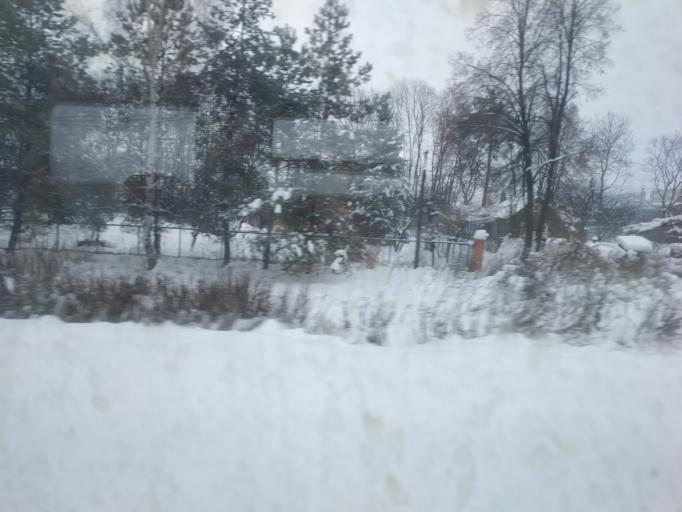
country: RU
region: Moskovskaya
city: Malyshevo
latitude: 55.4953
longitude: 38.3714
